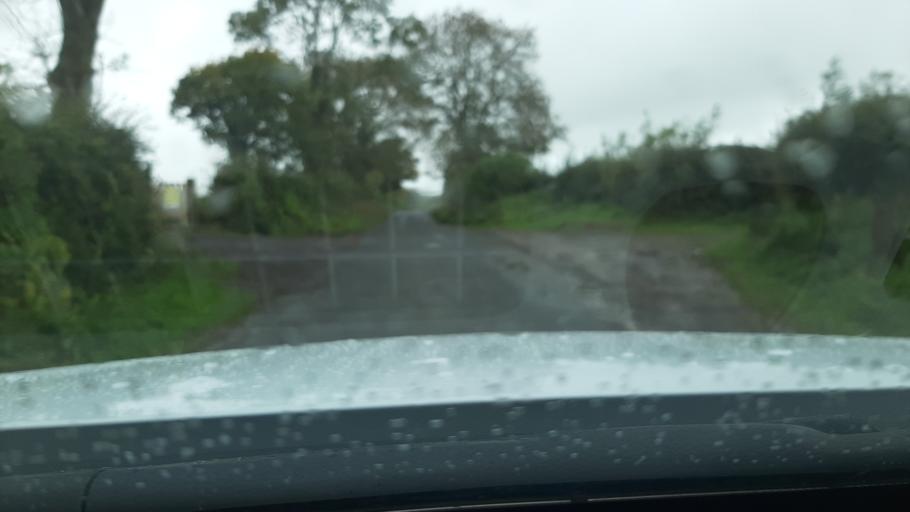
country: IE
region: Leinster
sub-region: Kildare
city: Kildare
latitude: 53.1753
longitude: -6.9238
